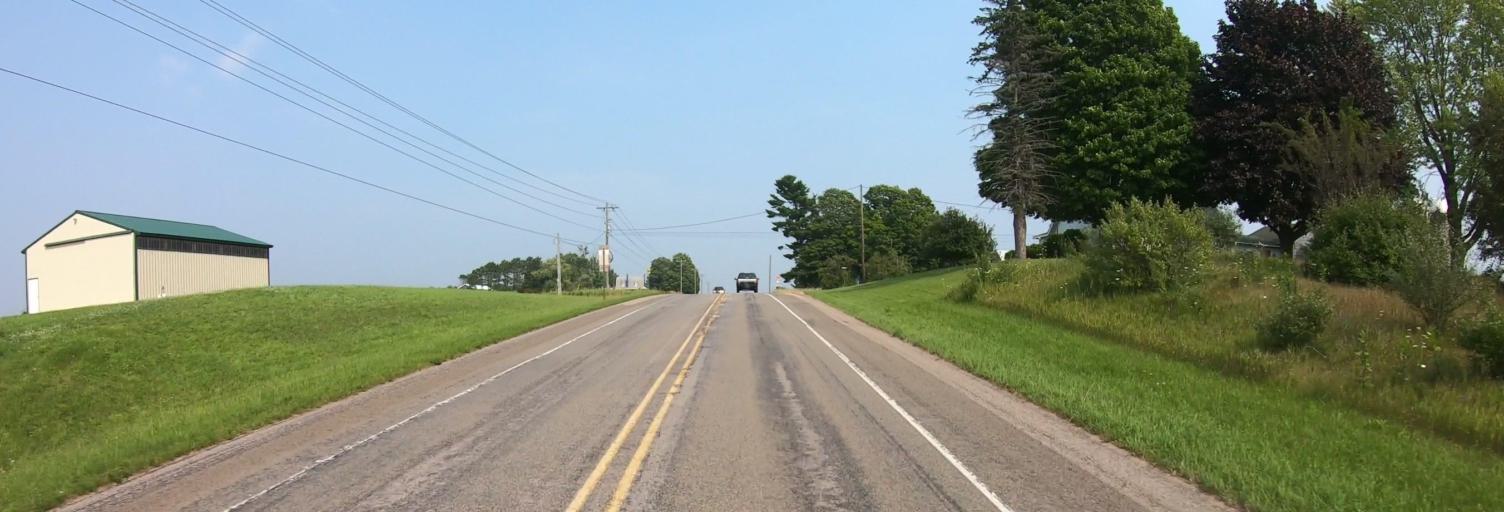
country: US
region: Michigan
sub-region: Charlevoix County
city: Charlevoix
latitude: 45.1849
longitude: -85.2999
